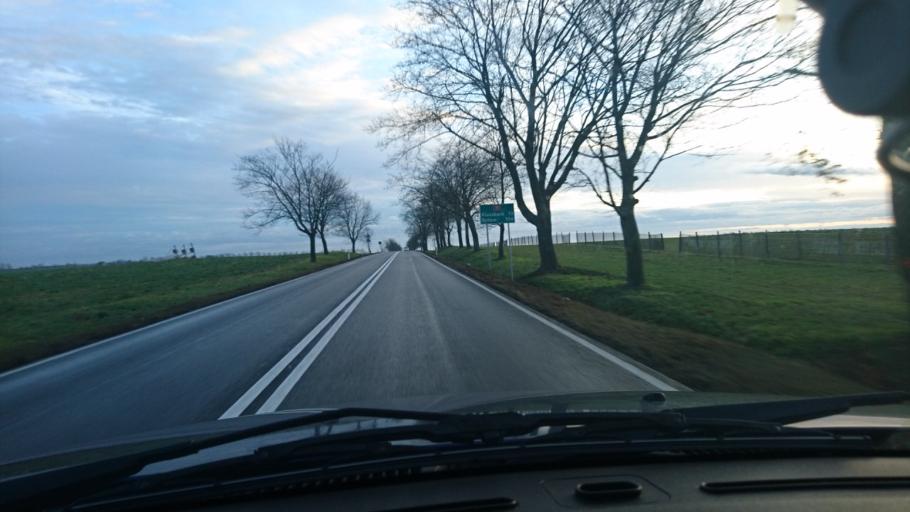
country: PL
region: Opole Voivodeship
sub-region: Powiat kluczborski
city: Byczyna
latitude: 51.0808
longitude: 18.1994
